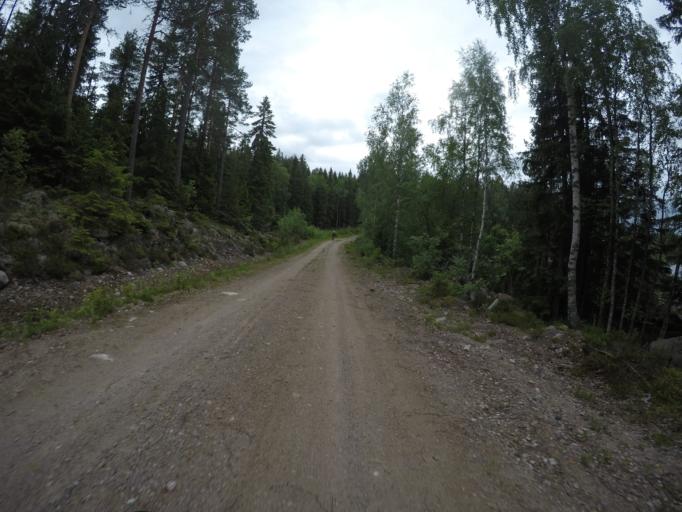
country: SE
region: Dalarna
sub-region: Ludvika Kommun
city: Abborrberget
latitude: 60.0715
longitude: 14.5640
